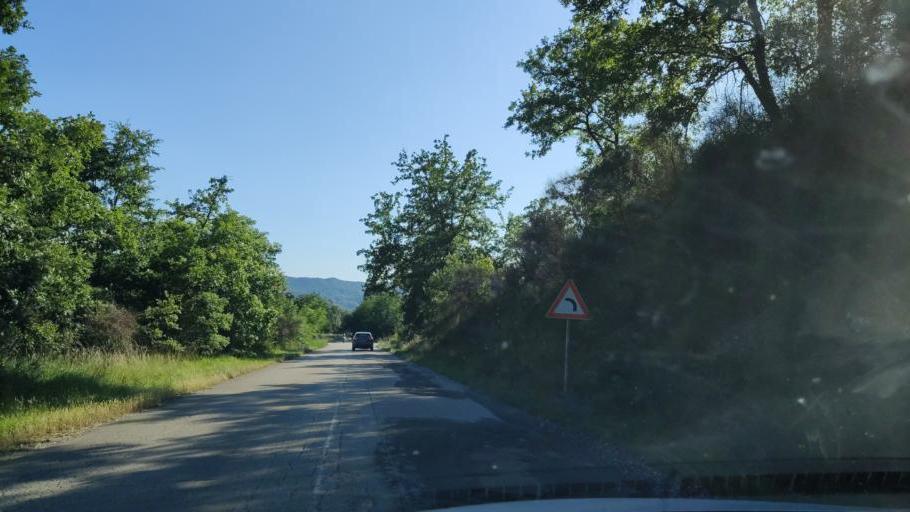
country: IT
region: Umbria
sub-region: Provincia di Terni
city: Penna in Teverina
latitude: 42.4805
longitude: 12.3656
